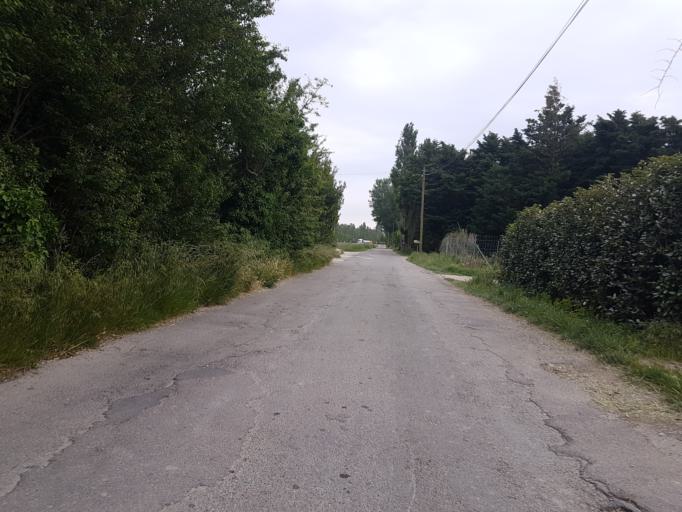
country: FR
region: Languedoc-Roussillon
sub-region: Departement du Gard
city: Roquemaure
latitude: 44.0598
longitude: 4.7773
